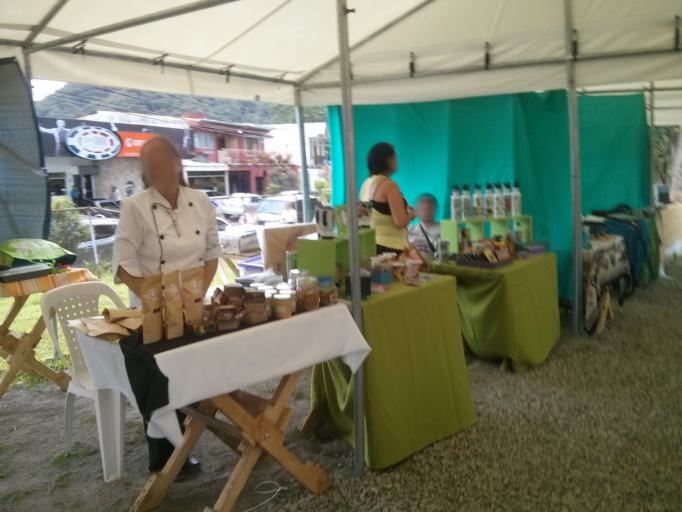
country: CR
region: San Jose
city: Curridabat
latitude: 9.9090
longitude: -84.0306
